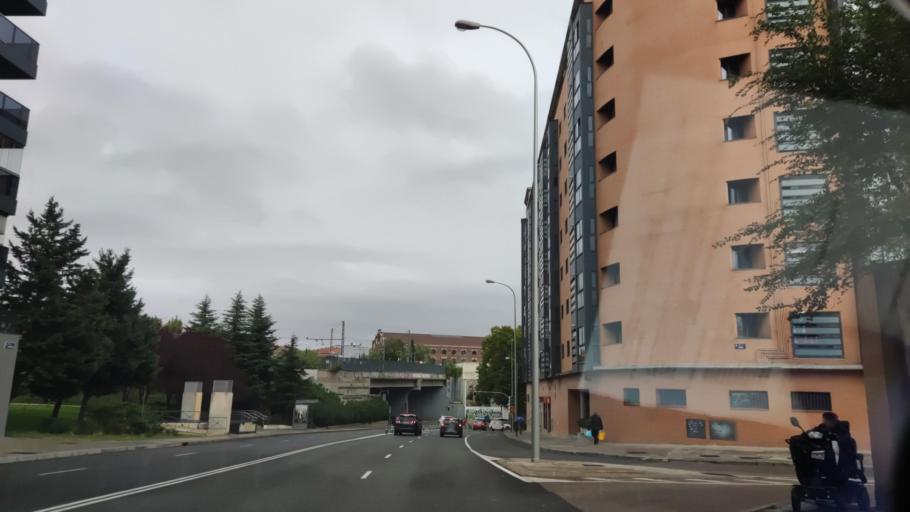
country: ES
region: Madrid
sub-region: Provincia de Madrid
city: Arganzuela
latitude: 40.3945
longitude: -3.6812
